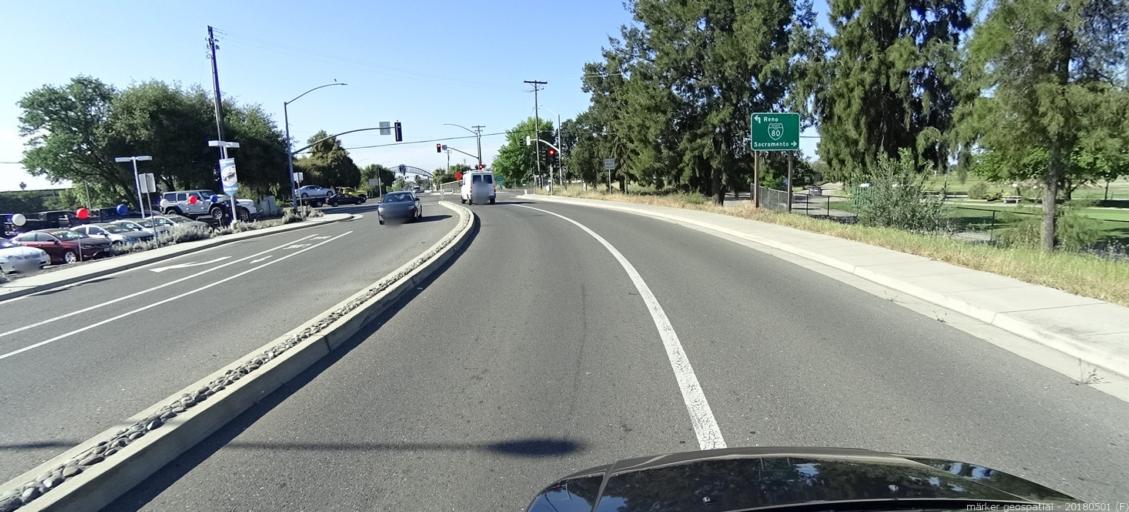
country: US
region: California
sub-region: Sacramento County
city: Arden-Arcade
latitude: 38.6320
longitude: -121.4014
